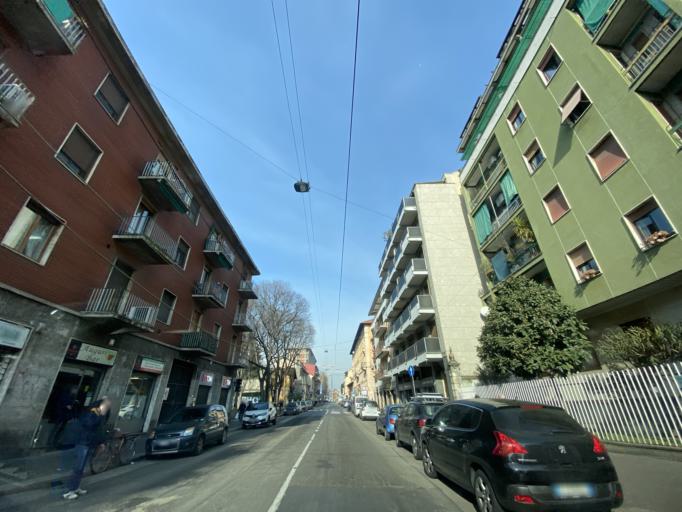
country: IT
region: Lombardy
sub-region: Citta metropolitana di Milano
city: Cormano
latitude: 45.5180
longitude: 9.1709
